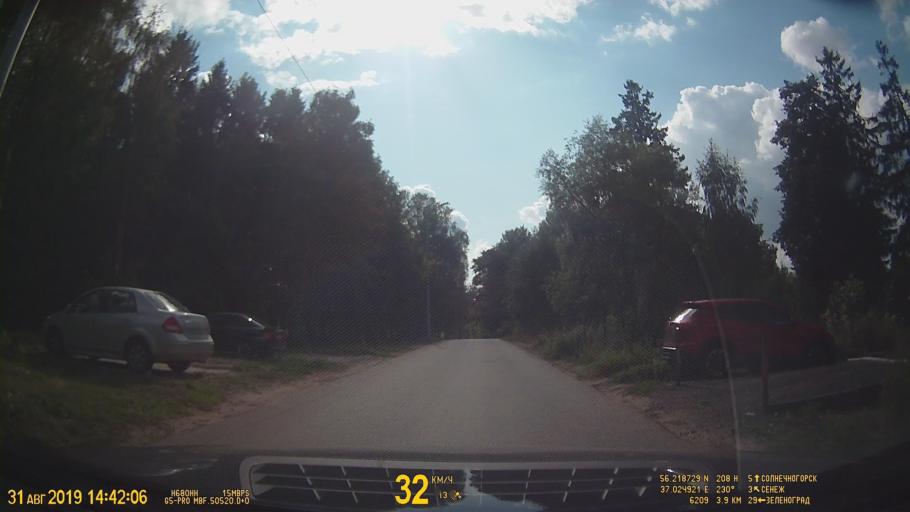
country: RU
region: Moskovskaya
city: Solnechnogorsk
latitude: 56.2187
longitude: 37.0245
